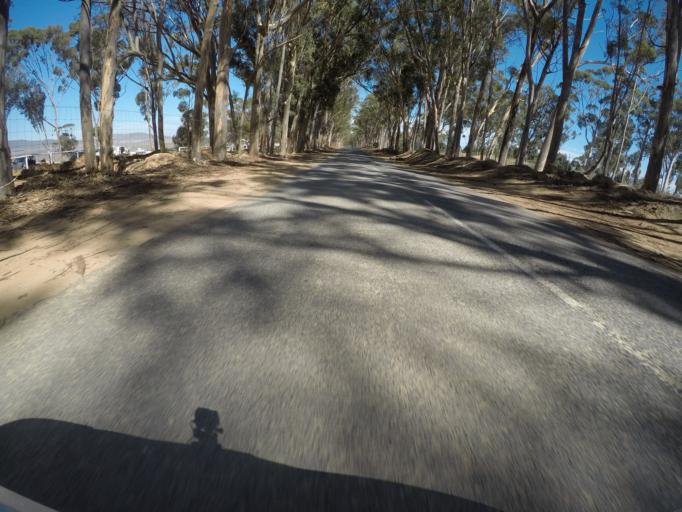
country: ZA
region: Western Cape
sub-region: City of Cape Town
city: Sunset Beach
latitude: -33.7611
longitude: 18.5527
